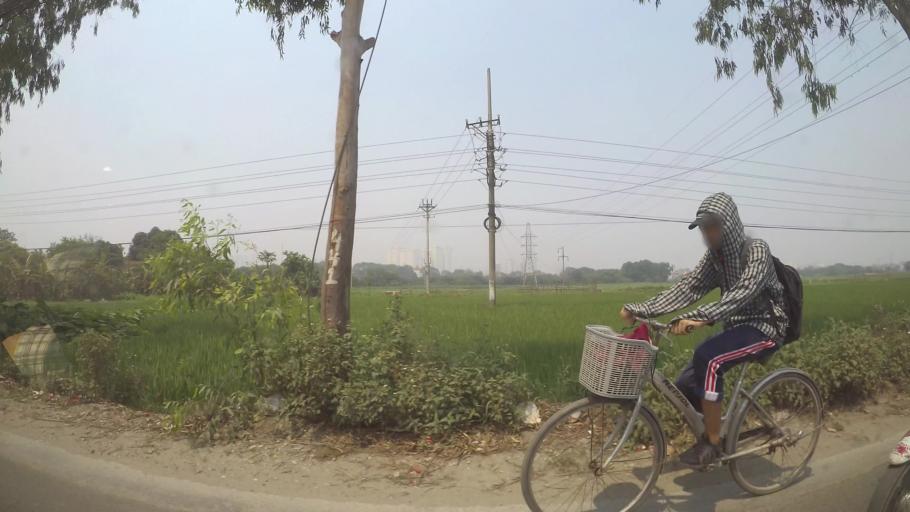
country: VN
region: Ha Noi
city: Van Dien
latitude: 20.9506
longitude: 105.8206
